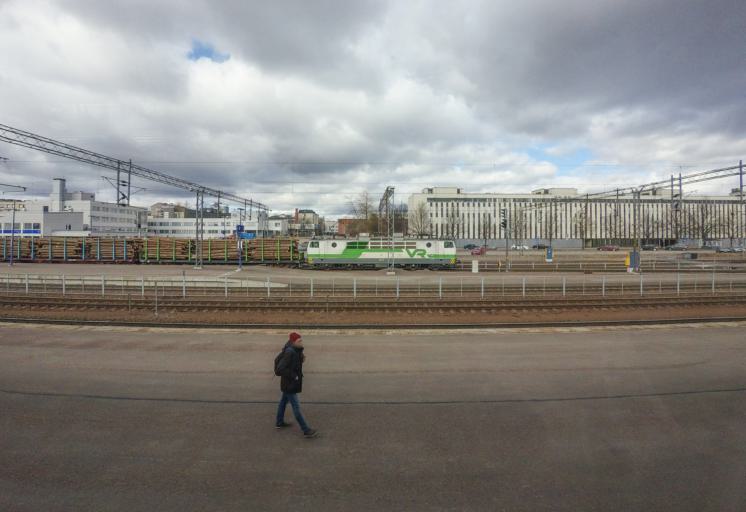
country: FI
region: Kymenlaakso
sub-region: Kouvola
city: Kouvola
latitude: 60.8656
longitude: 26.7069
